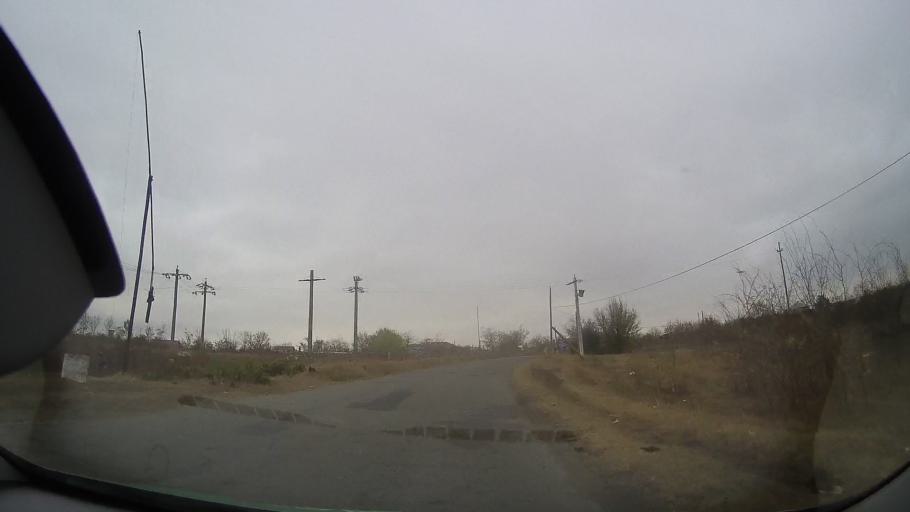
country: RO
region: Buzau
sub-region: Comuna Rusetu
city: Rusetu
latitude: 44.9532
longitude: 27.2186
